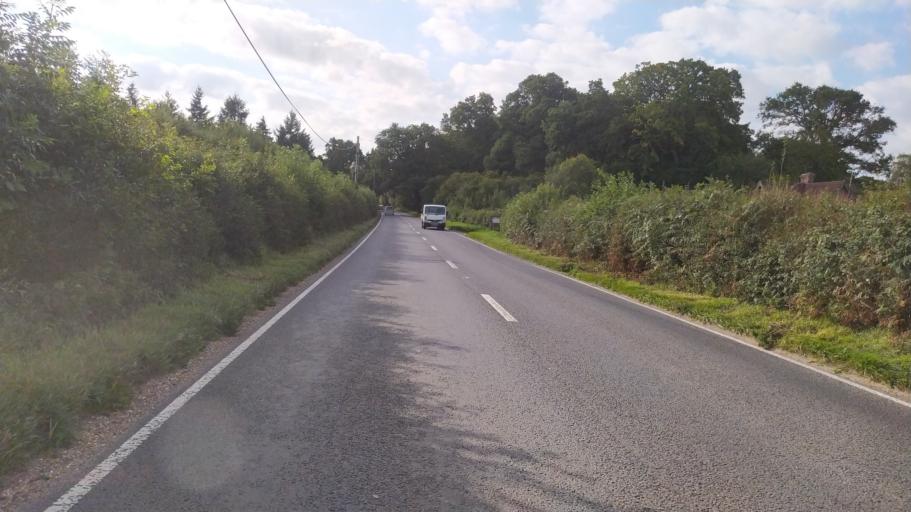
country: GB
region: England
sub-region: Dorset
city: Lytchett Matravers
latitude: 50.7774
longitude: -2.0704
